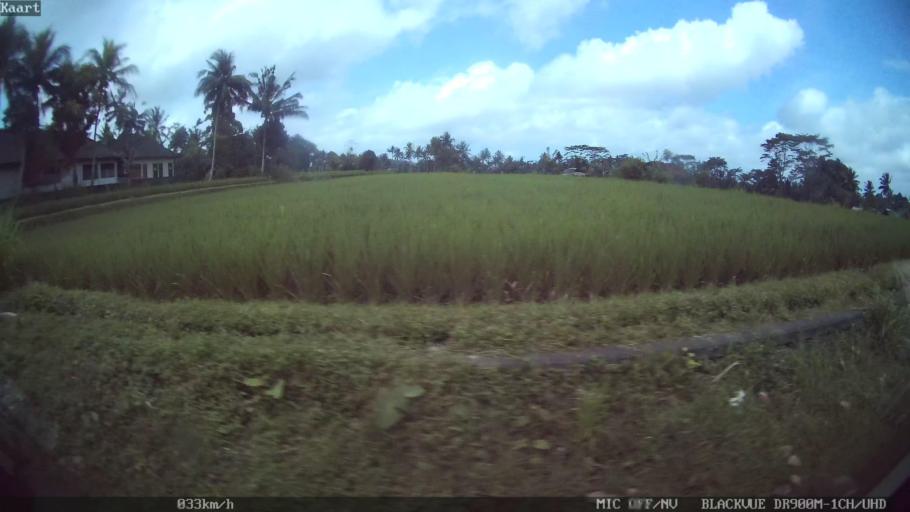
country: ID
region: Bali
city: Banjar Petak
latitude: -8.4529
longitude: 115.3182
